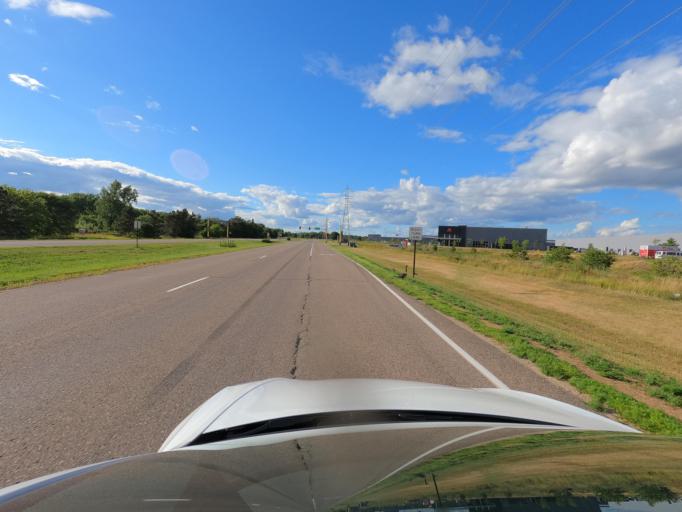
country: US
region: Minnesota
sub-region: Anoka County
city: Columbia Heights
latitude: 45.0535
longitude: -93.2781
